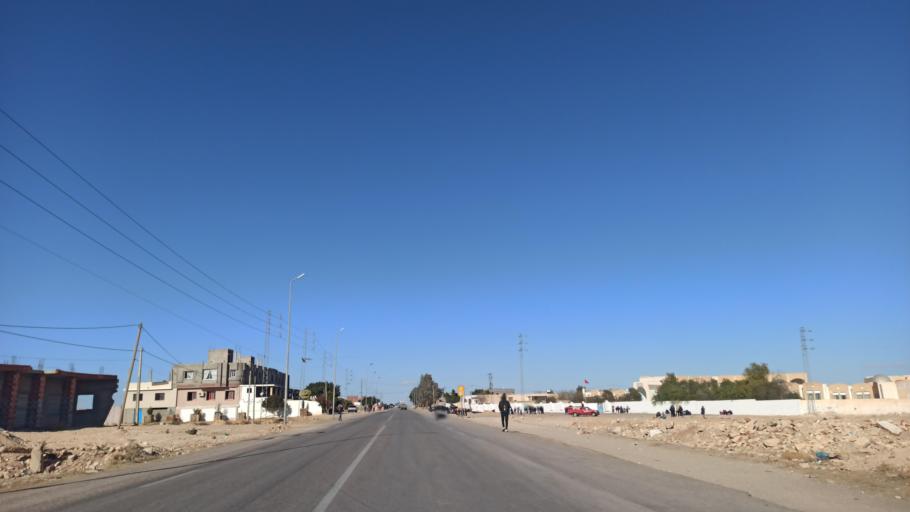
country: TN
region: Sidi Bu Zayd
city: Jilma
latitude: 35.2824
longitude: 9.4189
